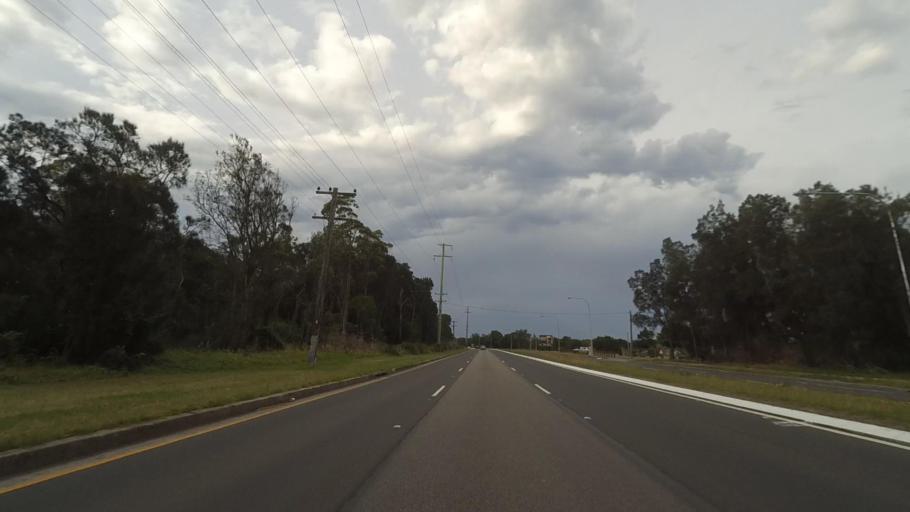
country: AU
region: New South Wales
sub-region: Shellharbour
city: Lake Illawarra
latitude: -34.5220
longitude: 150.8705
